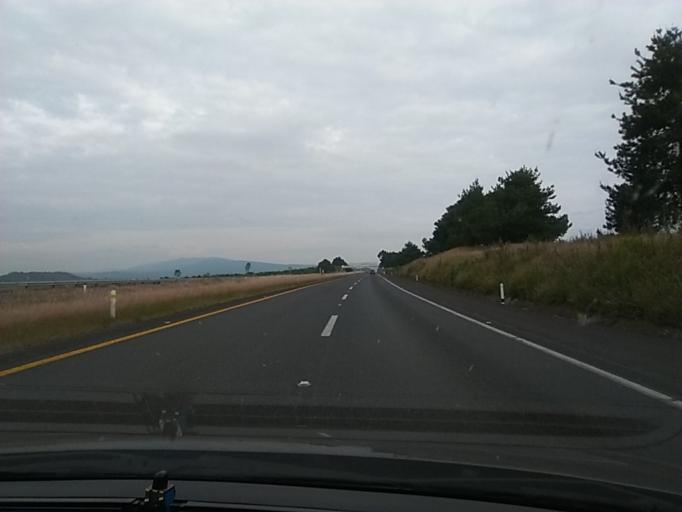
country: MX
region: Michoacan
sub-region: Puruandiro
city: San Lorenzo
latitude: 19.9601
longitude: -101.6697
